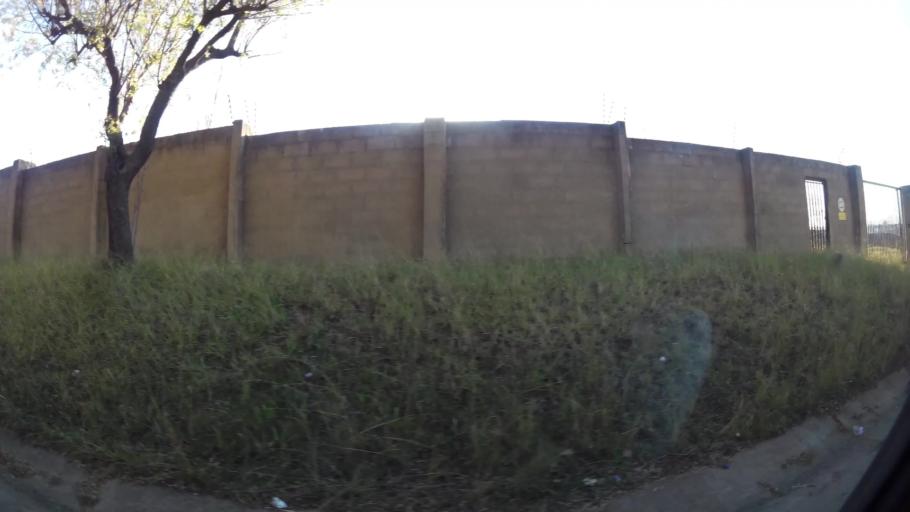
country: ZA
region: Gauteng
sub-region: City of Johannesburg Metropolitan Municipality
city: Midrand
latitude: -26.0291
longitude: 28.1520
